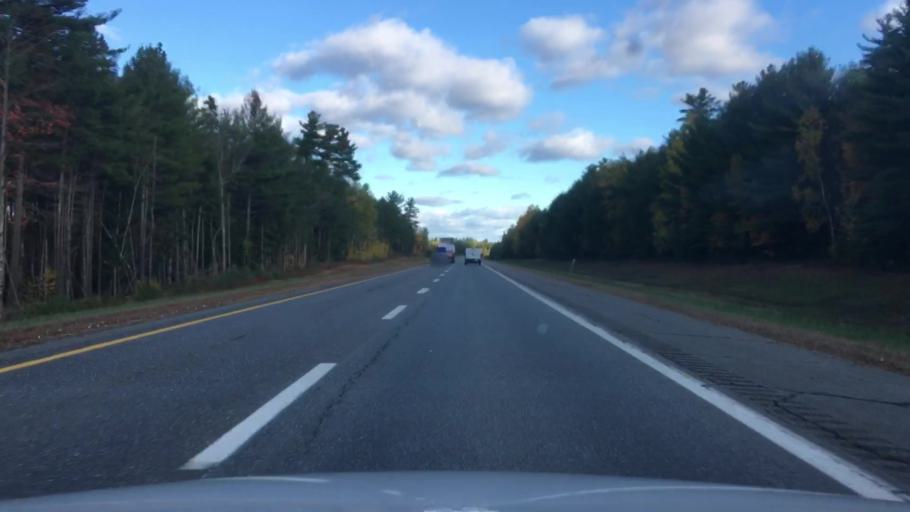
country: US
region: Maine
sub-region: Penobscot County
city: Greenbush
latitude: 45.1406
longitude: -68.7004
